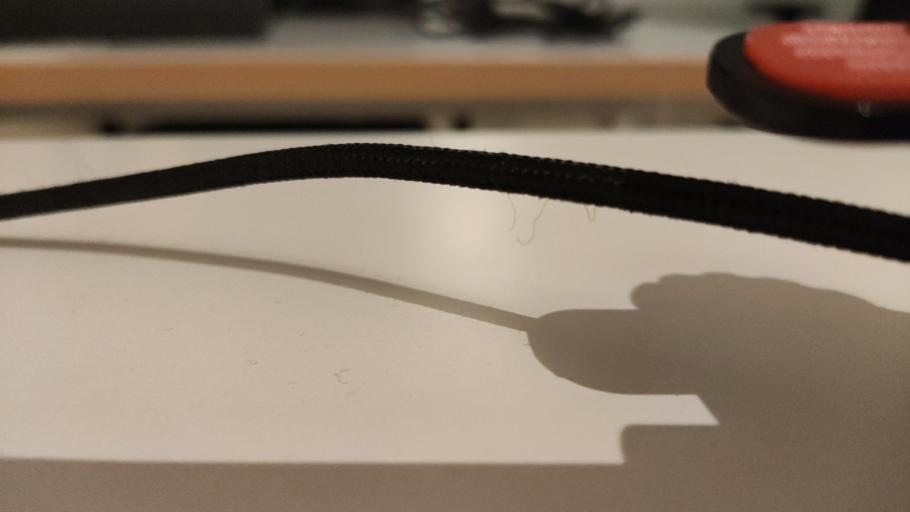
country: RU
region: Moskovskaya
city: Novoye
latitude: 55.6609
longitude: 38.9402
